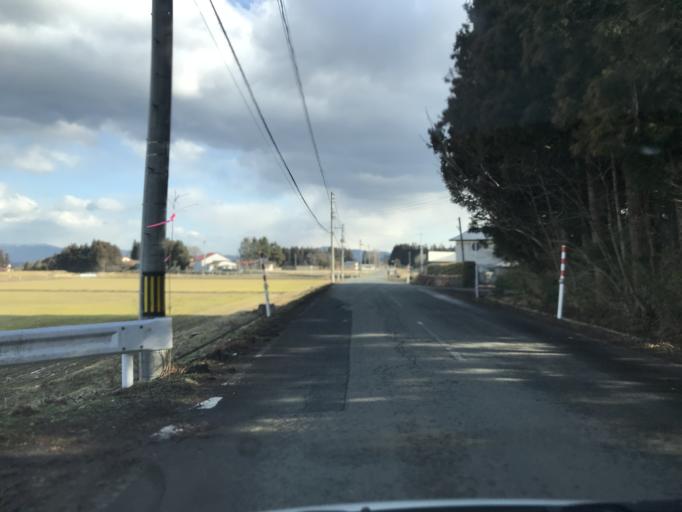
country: JP
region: Iwate
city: Mizusawa
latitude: 39.1015
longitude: 141.0257
